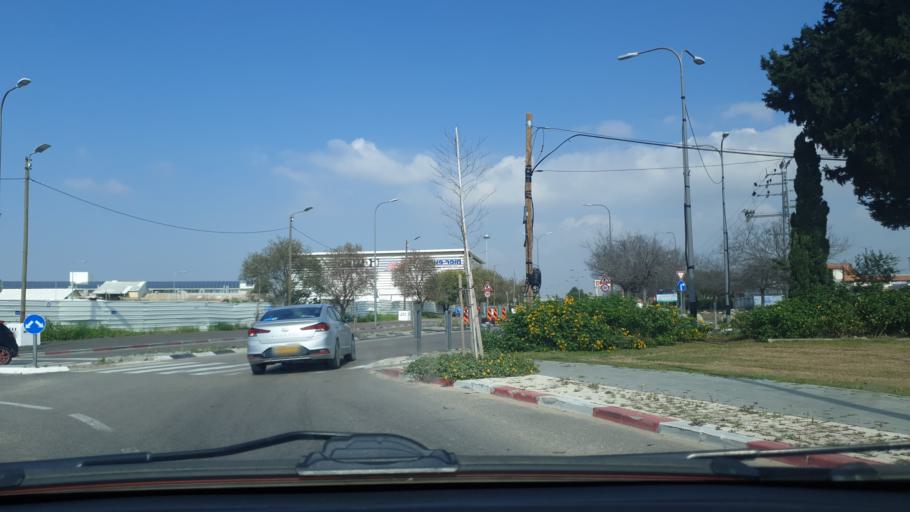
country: IL
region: Central District
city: Bet Dagan
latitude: 32.0040
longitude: 34.8060
